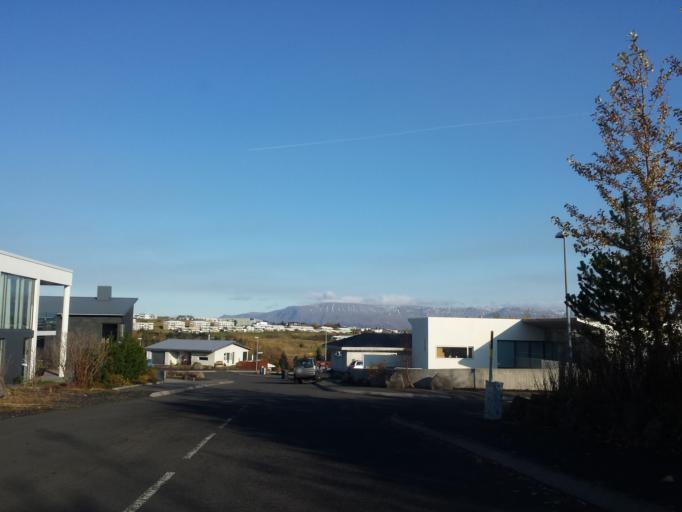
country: IS
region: Capital Region
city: Reykjavik
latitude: 64.0804
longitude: -21.8059
